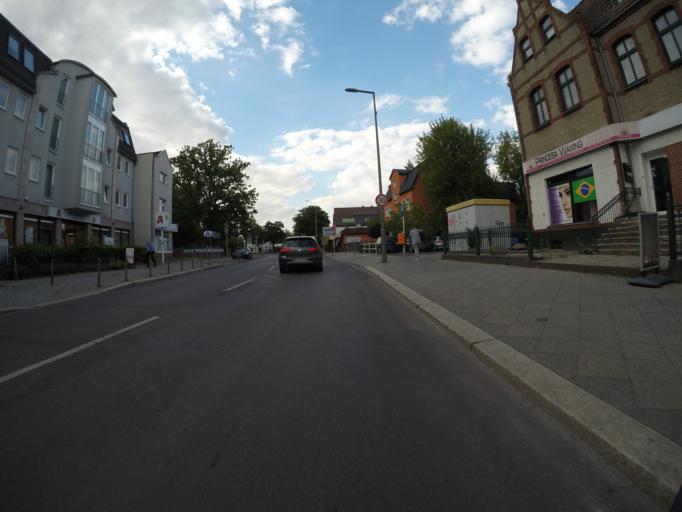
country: DE
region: Berlin
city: Mahlsdorf
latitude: 52.5132
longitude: 13.6123
